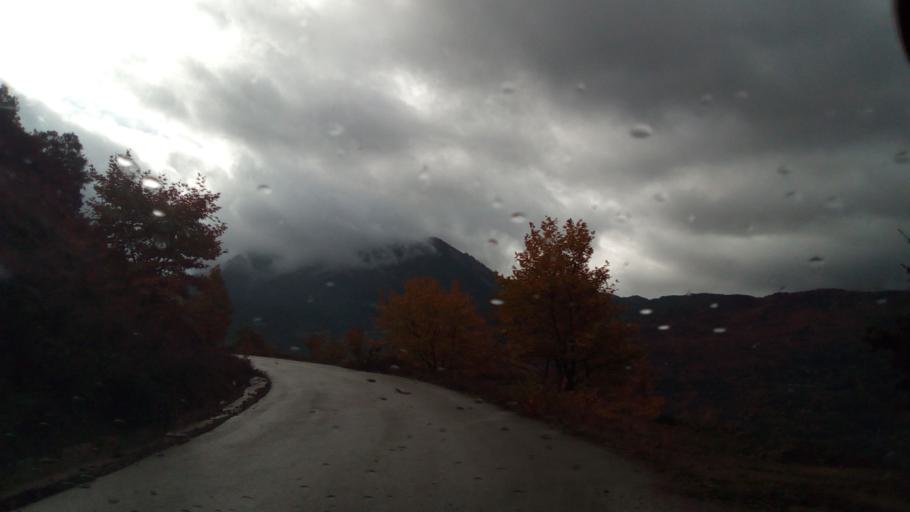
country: GR
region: West Greece
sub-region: Nomos Aitolias kai Akarnanias
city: Thermo
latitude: 38.6748
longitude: 21.8510
